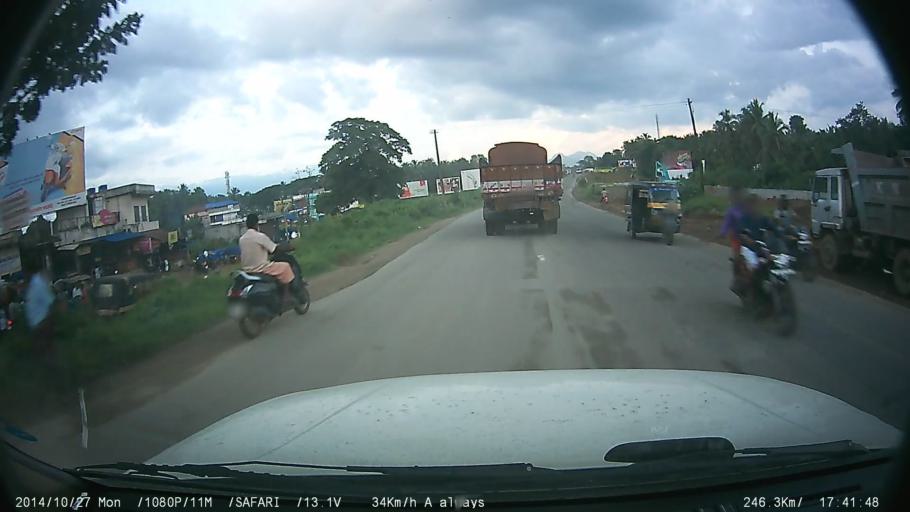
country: IN
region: Kerala
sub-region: Palakkad district
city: Palakkad
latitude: 10.7170
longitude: 76.5983
